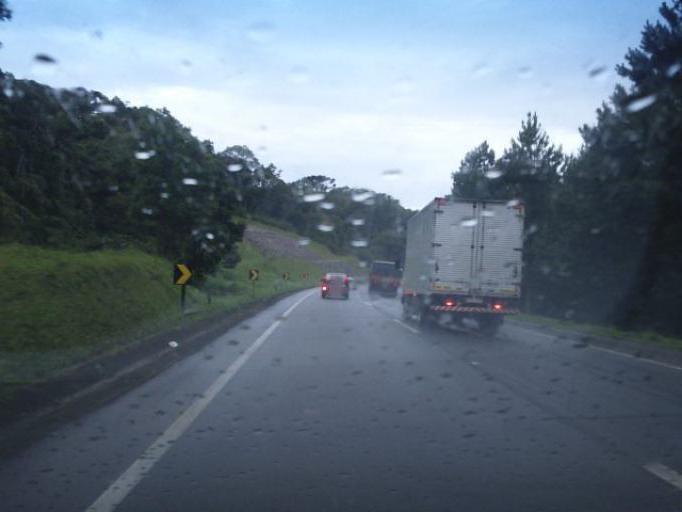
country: BR
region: Parana
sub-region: Sao Jose Dos Pinhais
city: Sao Jose dos Pinhais
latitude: -25.8414
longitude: -49.0405
